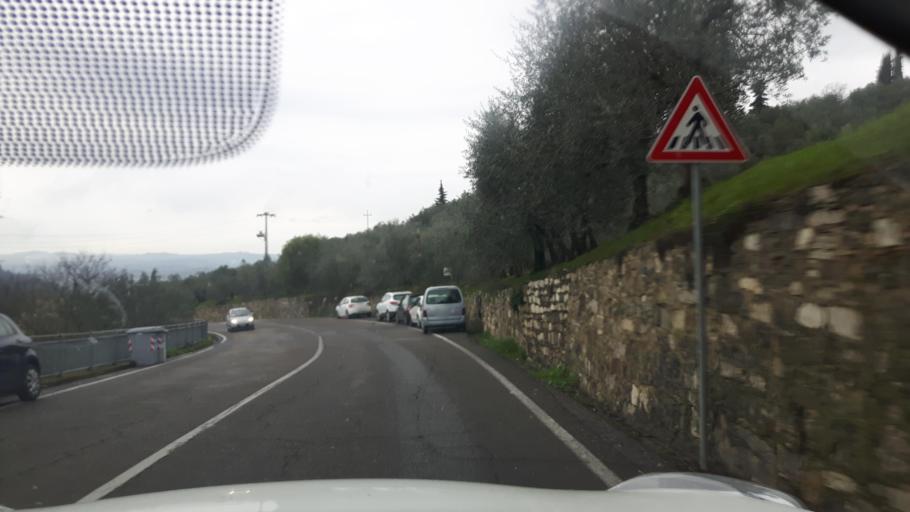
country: IT
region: Tuscany
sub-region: Province of Florence
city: Antella
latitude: 43.7323
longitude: 11.3670
